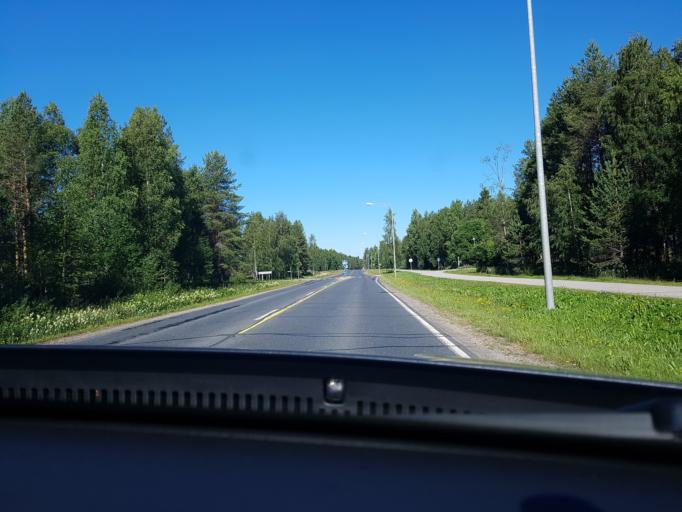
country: FI
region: Kainuu
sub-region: Kehys-Kainuu
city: Kuhmo
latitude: 64.1195
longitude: 29.5225
